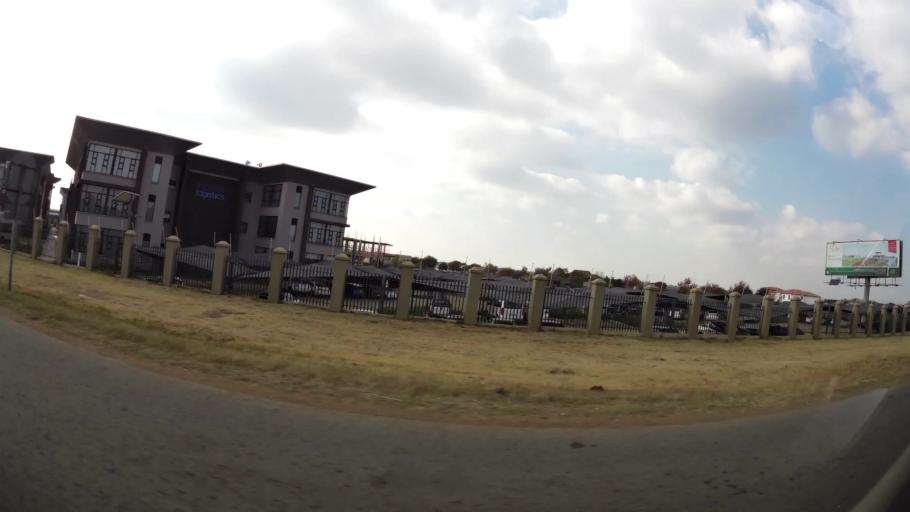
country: ZA
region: Gauteng
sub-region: Ekurhuleni Metropolitan Municipality
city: Benoni
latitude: -26.1417
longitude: 28.2691
